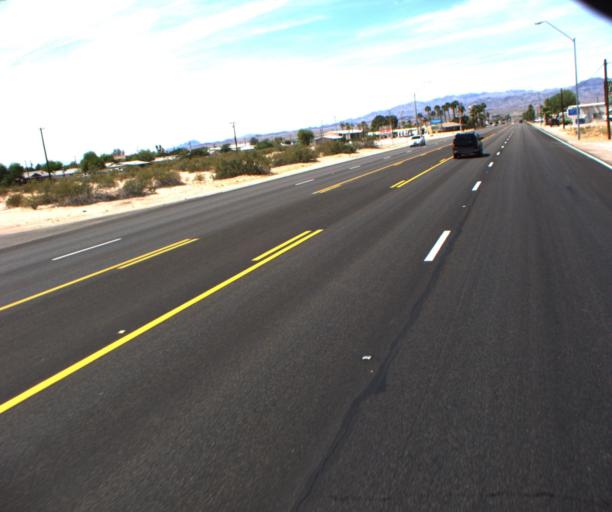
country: US
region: Arizona
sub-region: La Paz County
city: Parker
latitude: 34.1404
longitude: -114.2829
